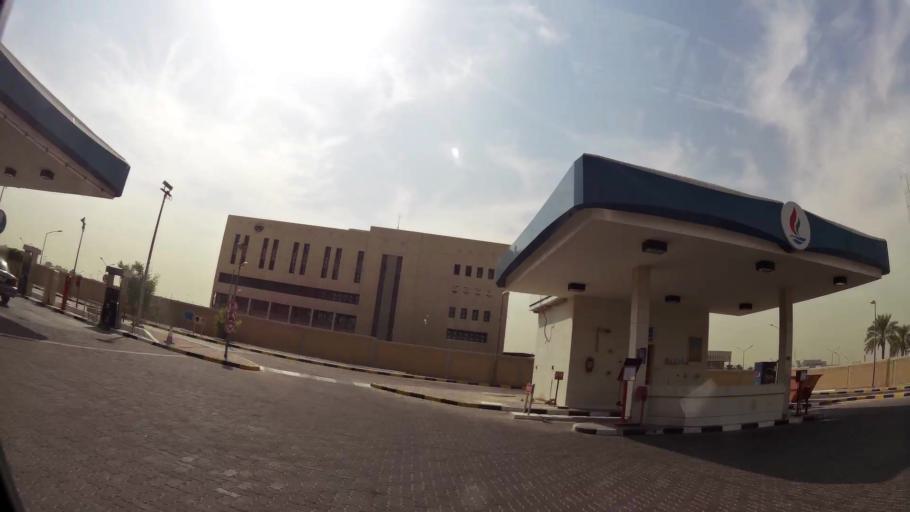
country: KW
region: Mubarak al Kabir
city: Sabah as Salim
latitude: 29.2709
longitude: 48.0189
